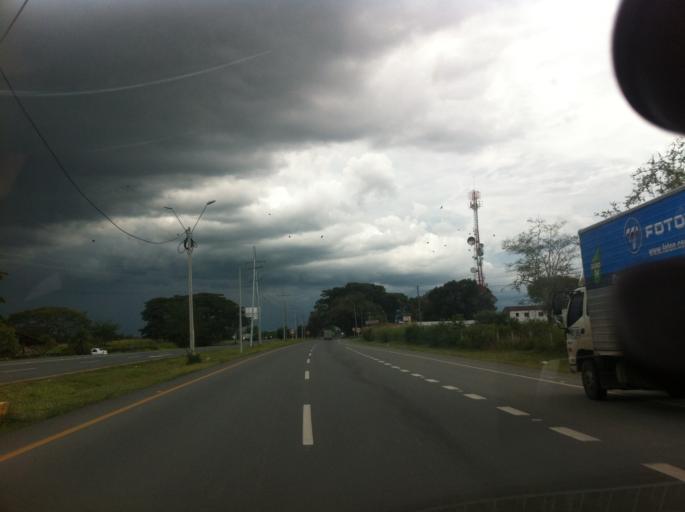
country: CO
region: Valle del Cauca
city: El Cerrito
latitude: 3.7003
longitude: -76.3181
